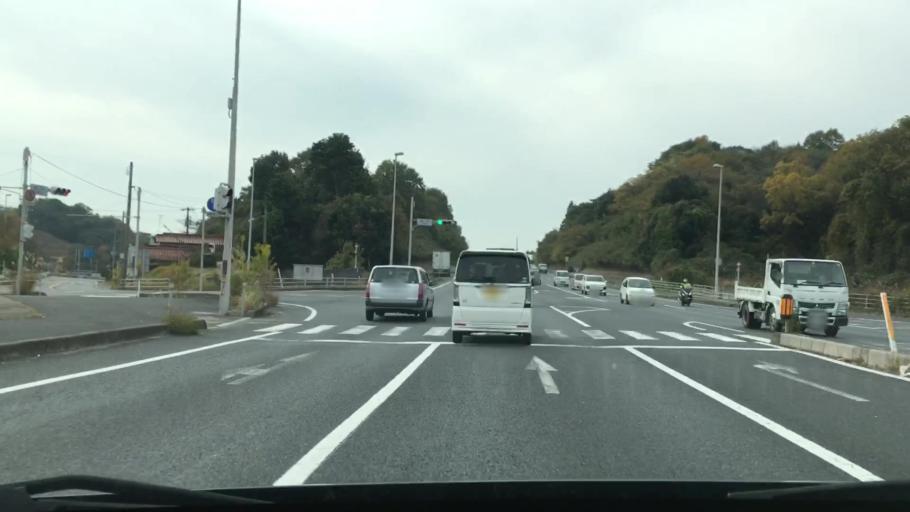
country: JP
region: Yamaguchi
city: Kudamatsu
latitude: 34.0320
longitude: 131.9256
